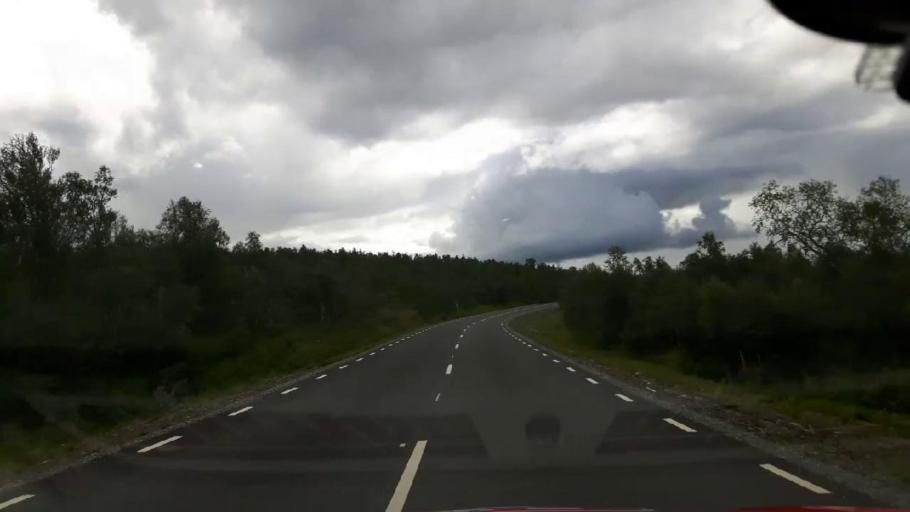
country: NO
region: Nord-Trondelag
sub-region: Royrvik
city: Royrvik
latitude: 64.9753
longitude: 14.2130
